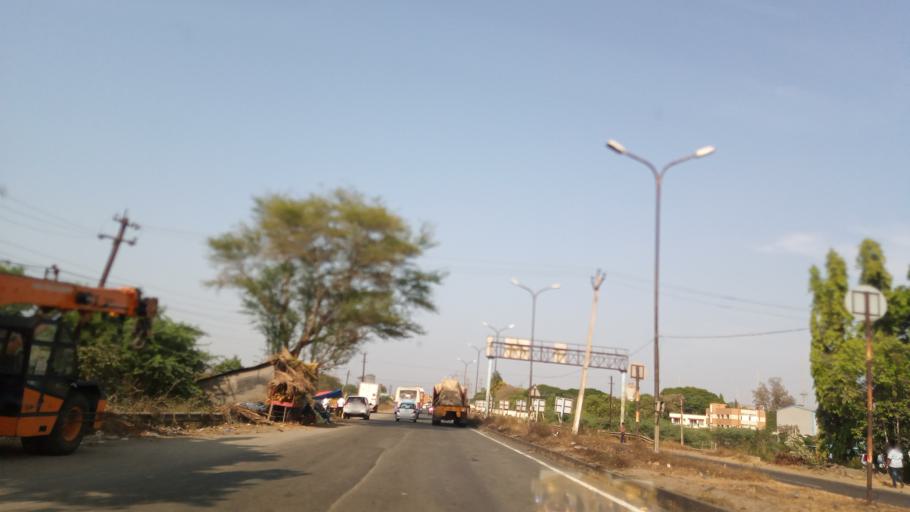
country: IN
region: Tamil Nadu
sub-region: Kancheepuram
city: Sriperumbudur
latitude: 12.9827
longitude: 79.9704
